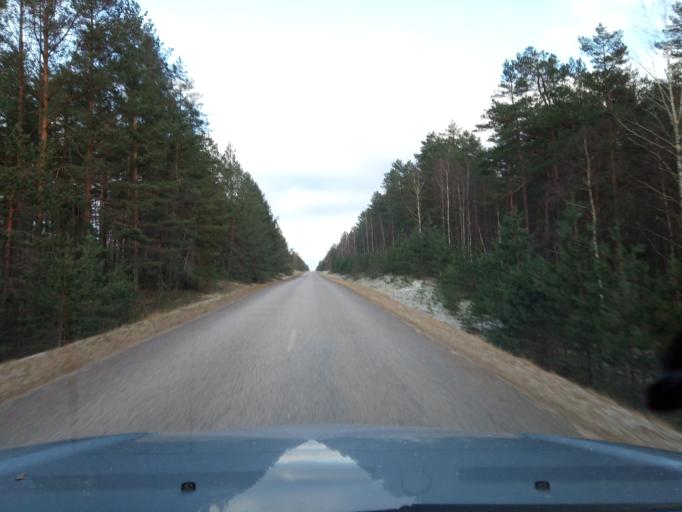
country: LT
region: Alytaus apskritis
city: Varena
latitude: 54.0841
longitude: 24.4047
